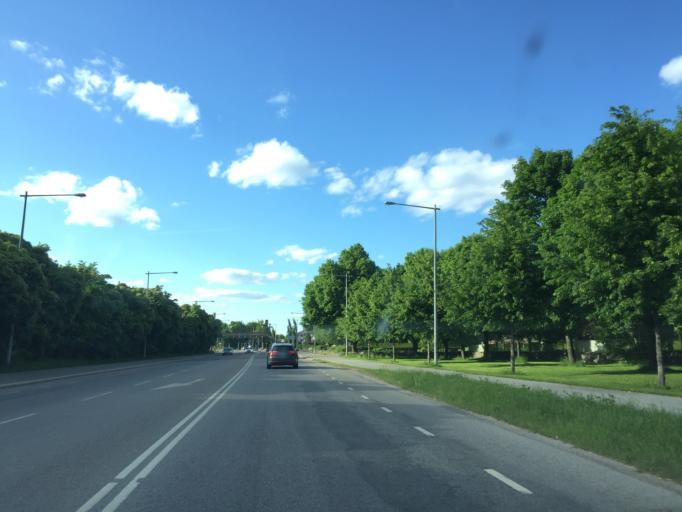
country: SE
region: OErebro
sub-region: Orebro Kommun
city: Orebro
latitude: 59.2566
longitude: 15.2415
